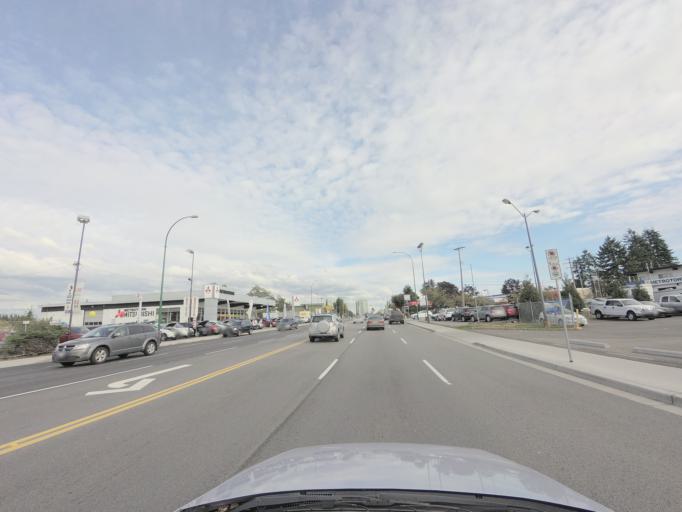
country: CA
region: British Columbia
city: Burnaby
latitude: 49.2211
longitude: -122.9769
